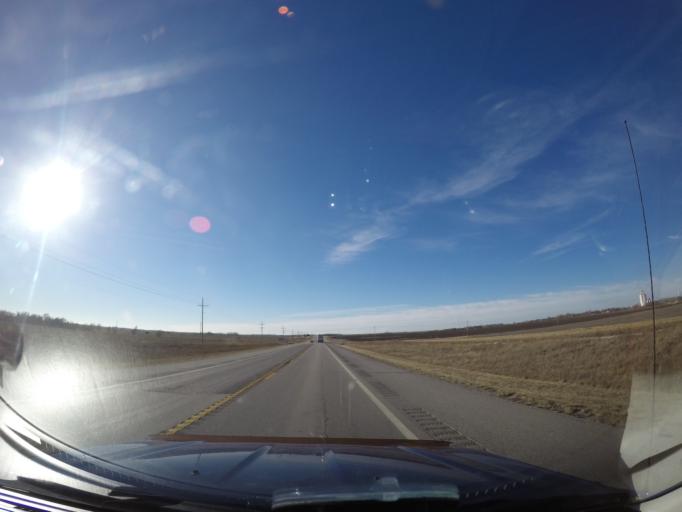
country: US
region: Kansas
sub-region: Marion County
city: Hillsboro
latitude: 38.3622
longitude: -97.2959
